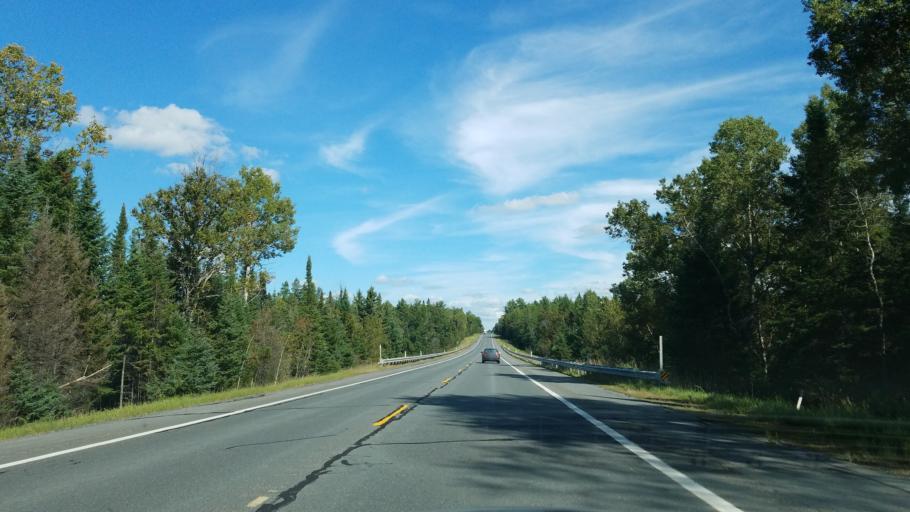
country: US
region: Michigan
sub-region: Baraga County
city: L'Anse
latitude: 46.5788
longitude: -88.4160
